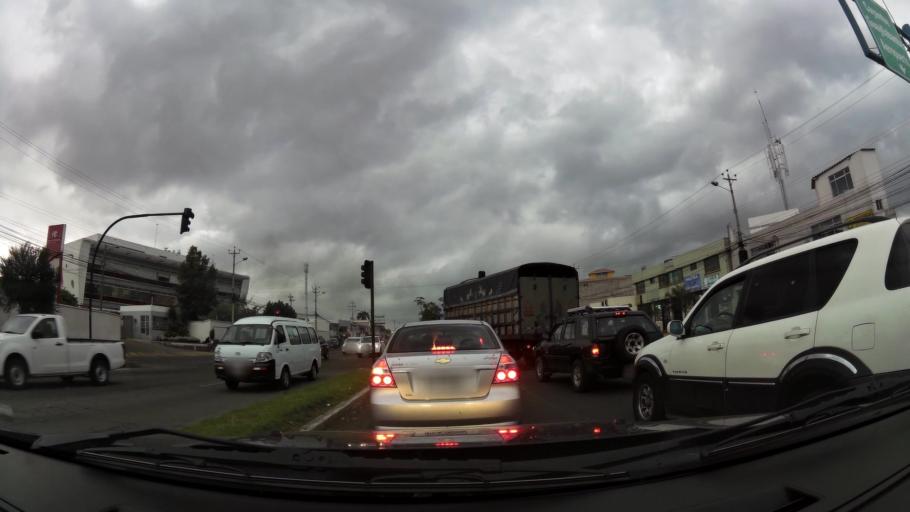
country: EC
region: Pichincha
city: Quito
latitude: -0.1071
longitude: -78.4440
